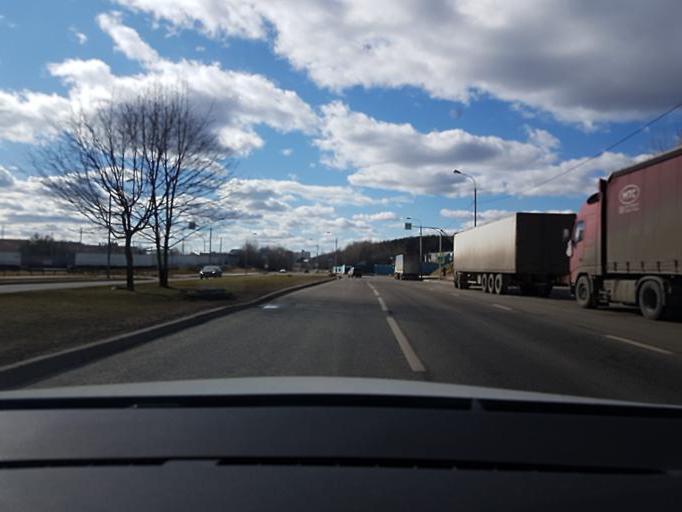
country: RU
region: Moskovskaya
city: Pavshino
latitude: 55.8401
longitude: 37.3474
